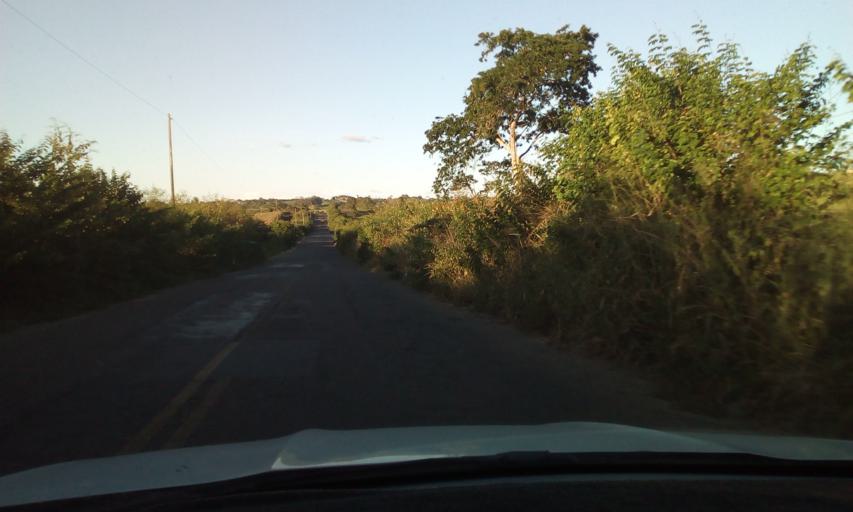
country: BR
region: Paraiba
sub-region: Areia
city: Remigio
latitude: -6.9601
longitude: -35.7907
